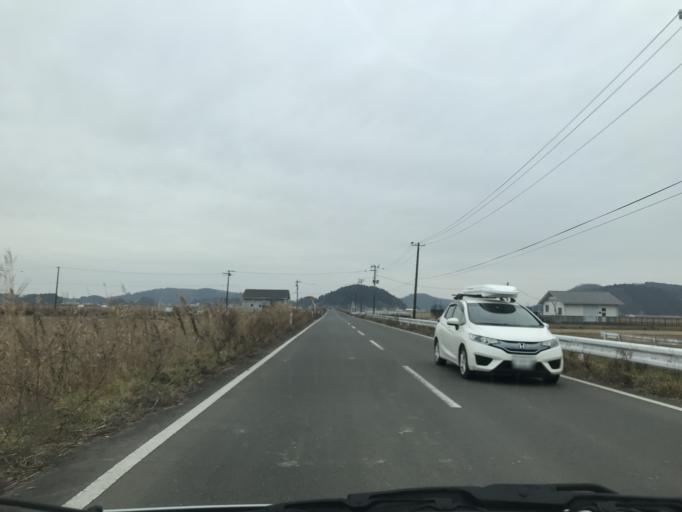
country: JP
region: Iwate
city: Ichinoseki
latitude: 38.7458
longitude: 141.2390
